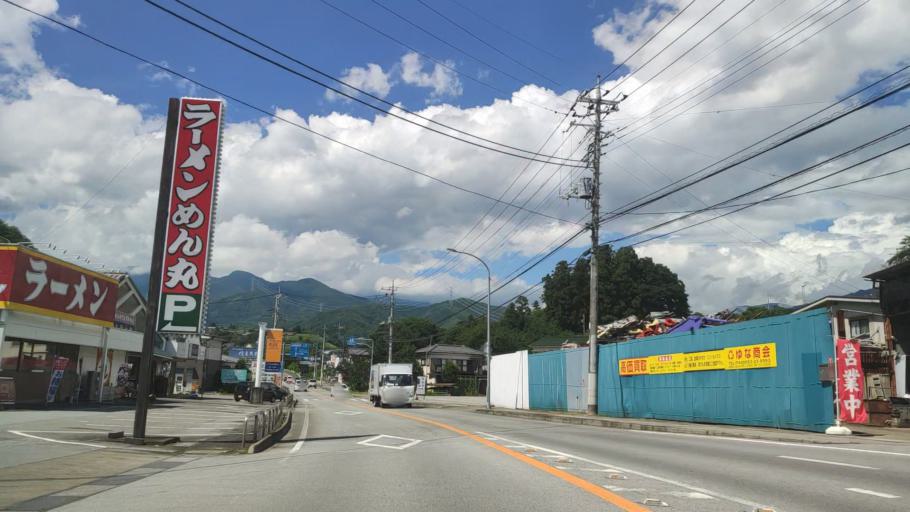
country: JP
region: Yamanashi
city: Enzan
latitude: 35.7322
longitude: 138.7120
